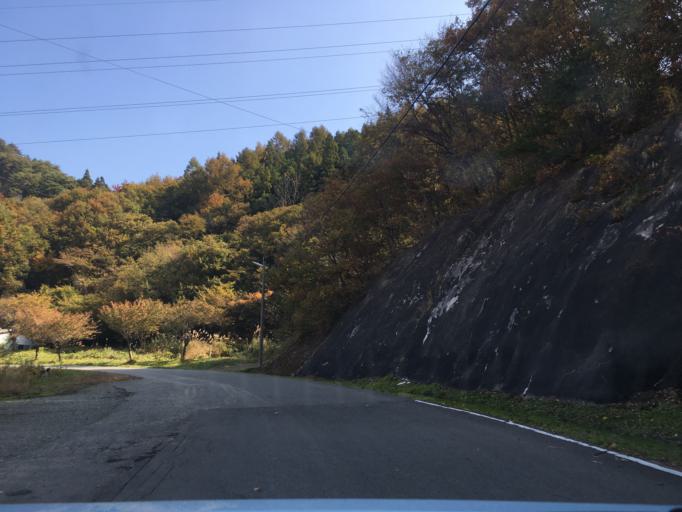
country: JP
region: Fukushima
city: Inawashiro
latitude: 37.4776
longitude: 140.0189
